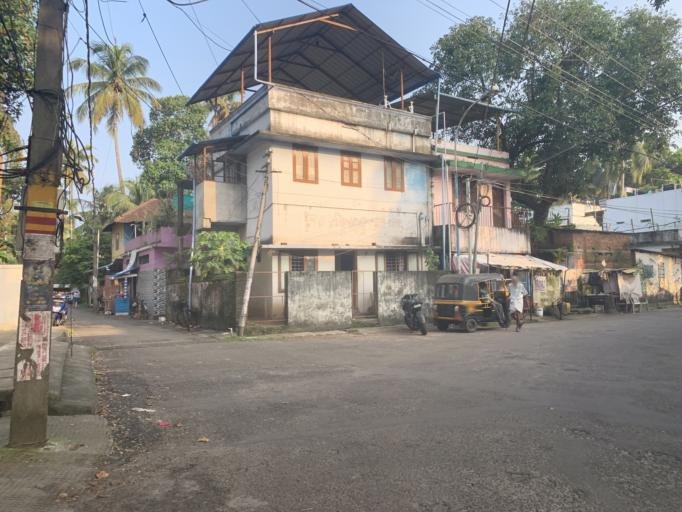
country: IN
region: Kerala
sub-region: Ernakulam
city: Cochin
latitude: 9.9593
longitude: 76.2496
